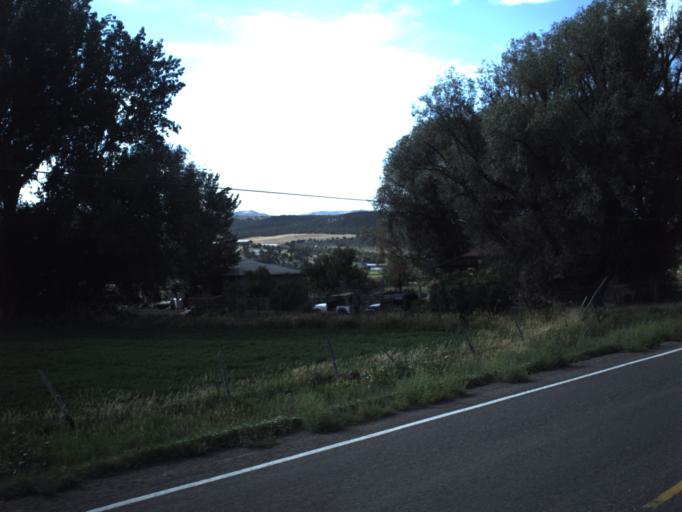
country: US
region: Utah
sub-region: Sanpete County
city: Fairview
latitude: 39.6009
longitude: -111.4447
